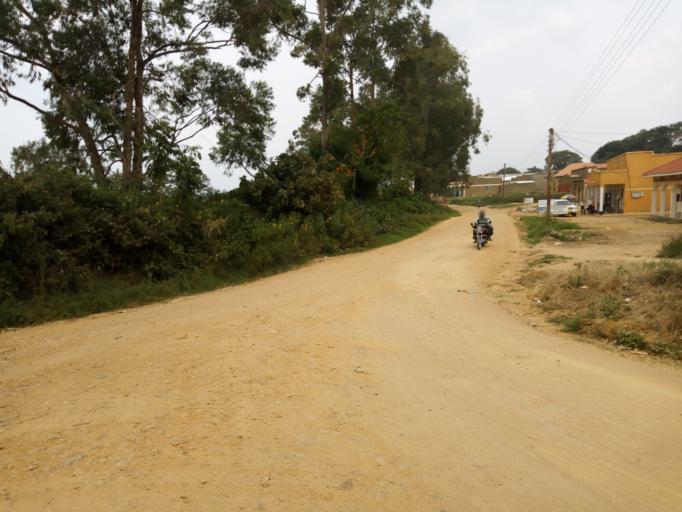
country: UG
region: Western Region
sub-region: Kanungu District
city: Ntungamo
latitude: -0.7466
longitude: 29.6962
